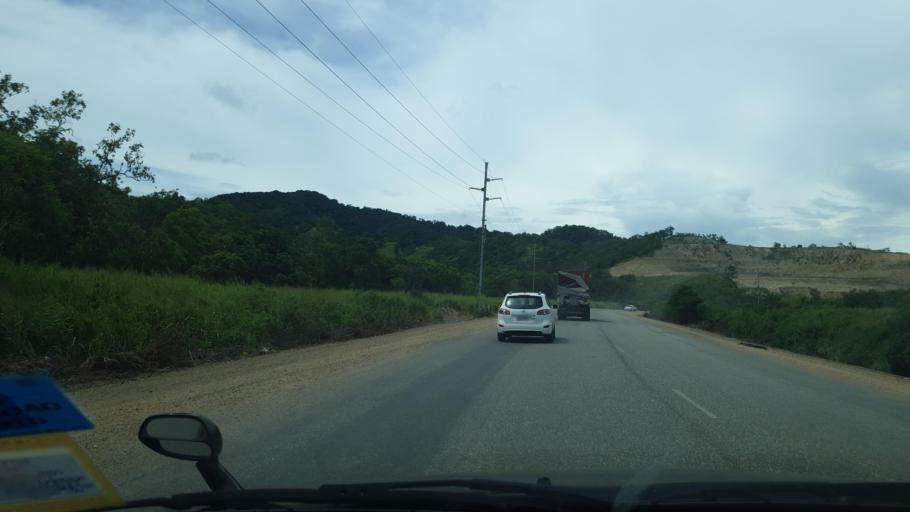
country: PG
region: National Capital
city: Port Moresby
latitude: -9.4173
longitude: 147.0997
